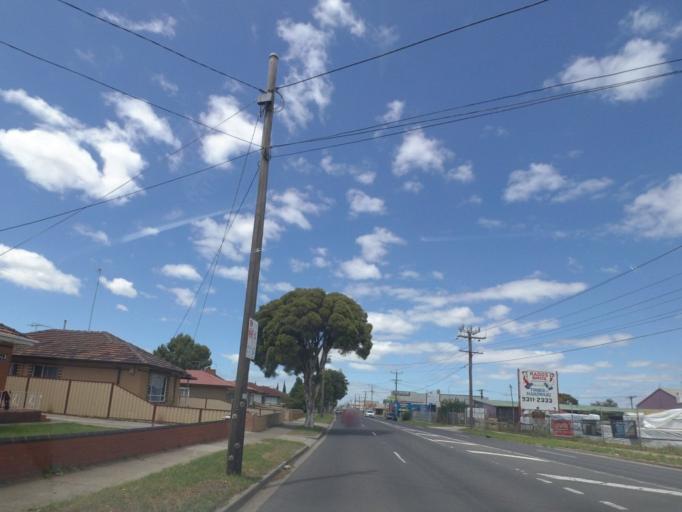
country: AU
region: Victoria
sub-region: Brimbank
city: Albion
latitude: -37.7658
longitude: 144.8309
